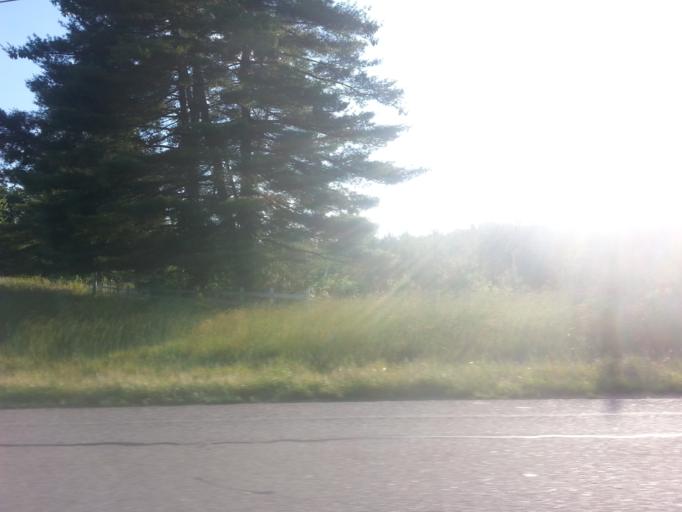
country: US
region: Georgia
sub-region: Union County
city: Blairsville
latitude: 34.9002
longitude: -84.0064
